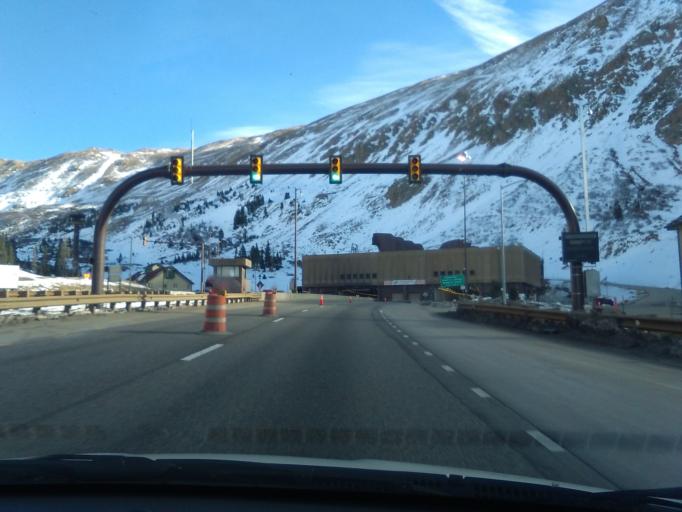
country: US
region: Colorado
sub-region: Summit County
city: Keystone
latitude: 39.6782
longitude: -105.9377
